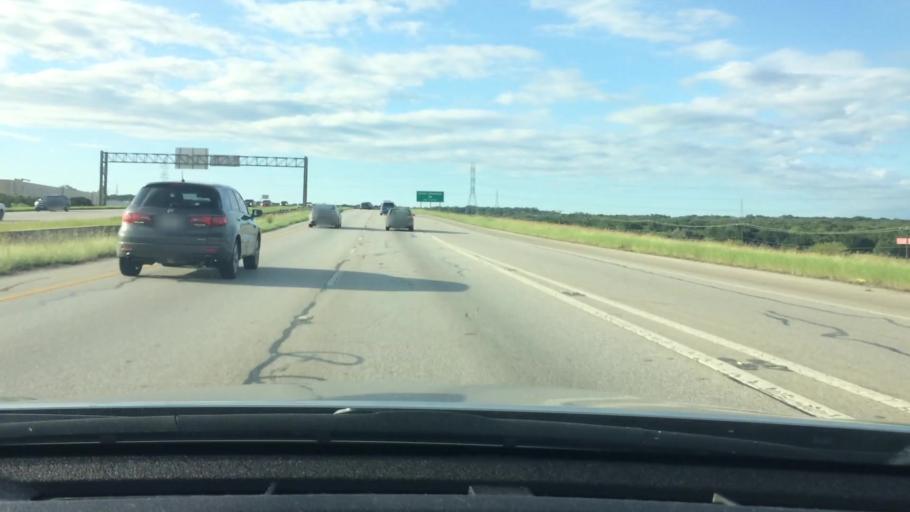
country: US
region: Texas
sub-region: Bexar County
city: Live Oak
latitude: 29.5975
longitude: -98.3557
